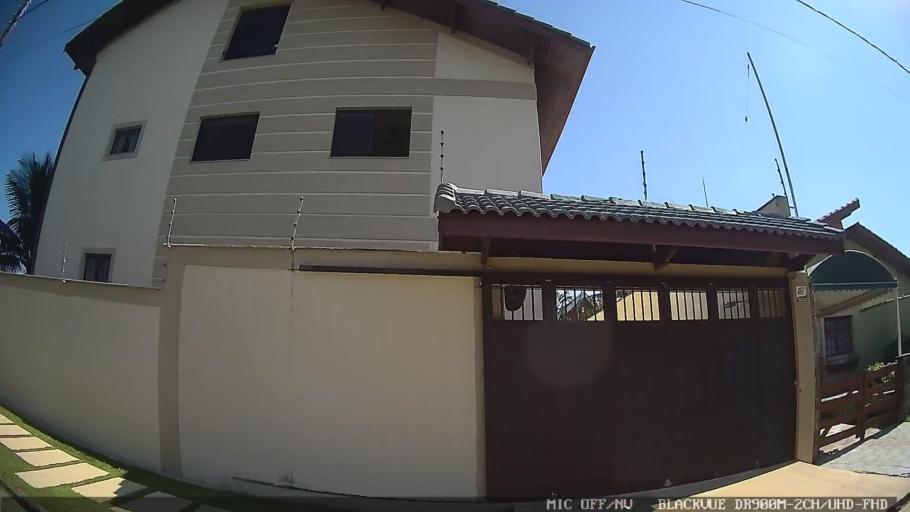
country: BR
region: Sao Paulo
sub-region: Peruibe
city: Peruibe
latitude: -24.2959
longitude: -46.9632
